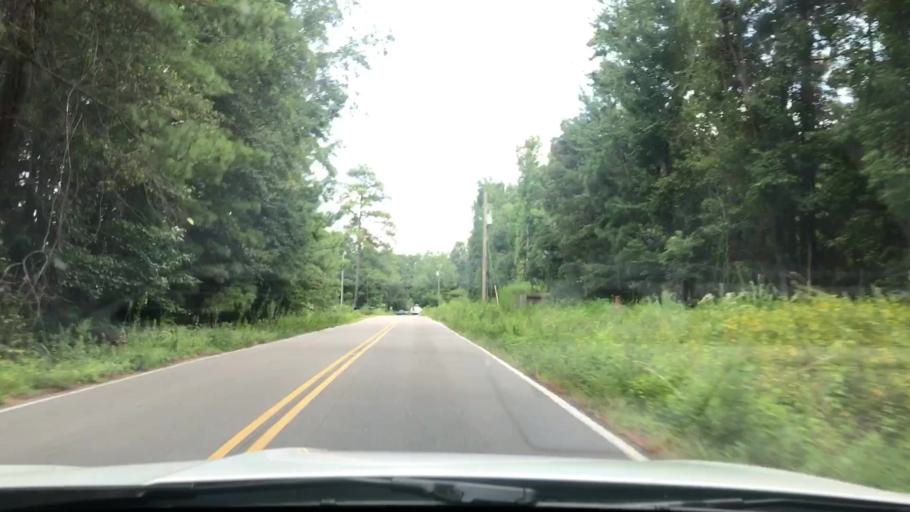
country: US
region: South Carolina
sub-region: Dorchester County
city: Summerville
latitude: 33.0341
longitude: -80.2118
